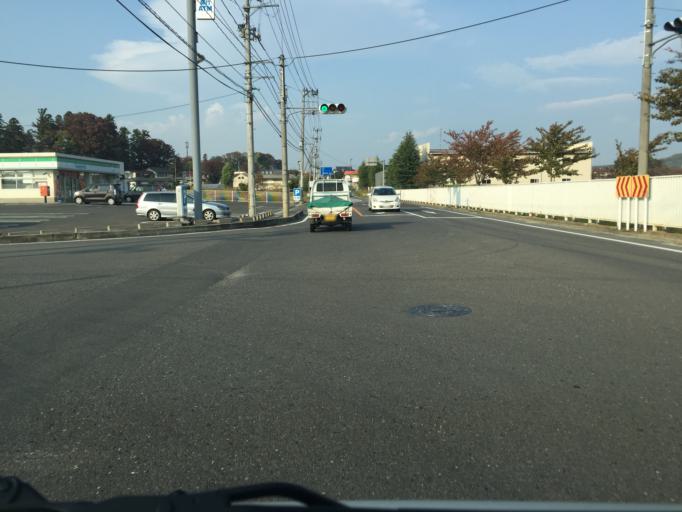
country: JP
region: Fukushima
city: Motomiya
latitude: 37.4886
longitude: 140.4006
